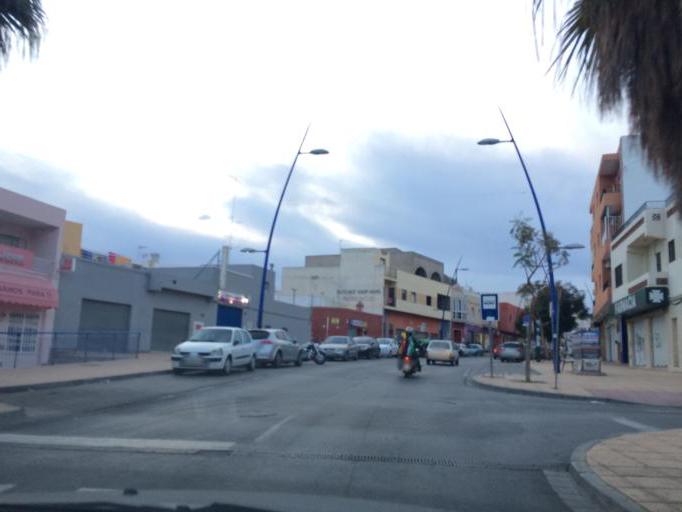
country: ES
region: Andalusia
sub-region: Provincia de Almeria
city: Viator
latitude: 36.8404
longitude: -2.4047
